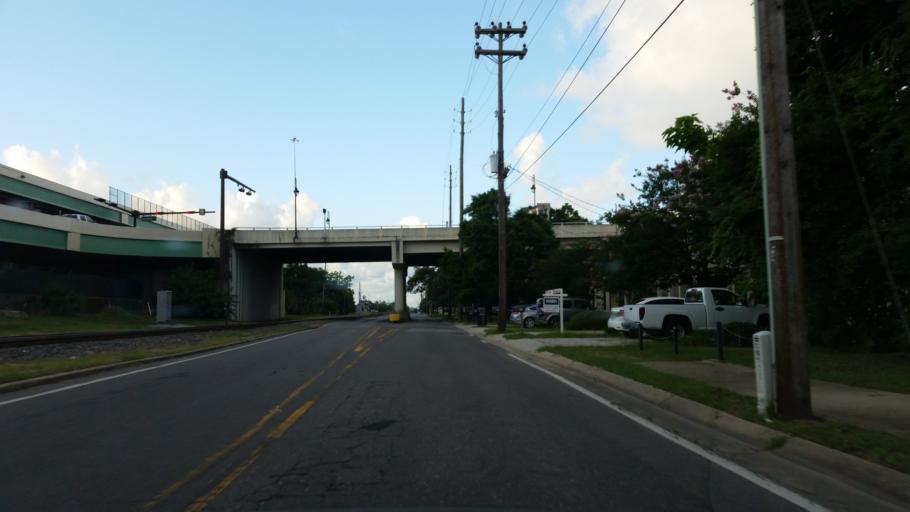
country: US
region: Florida
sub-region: Escambia County
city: Pensacola
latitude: 30.4226
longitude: -87.2149
